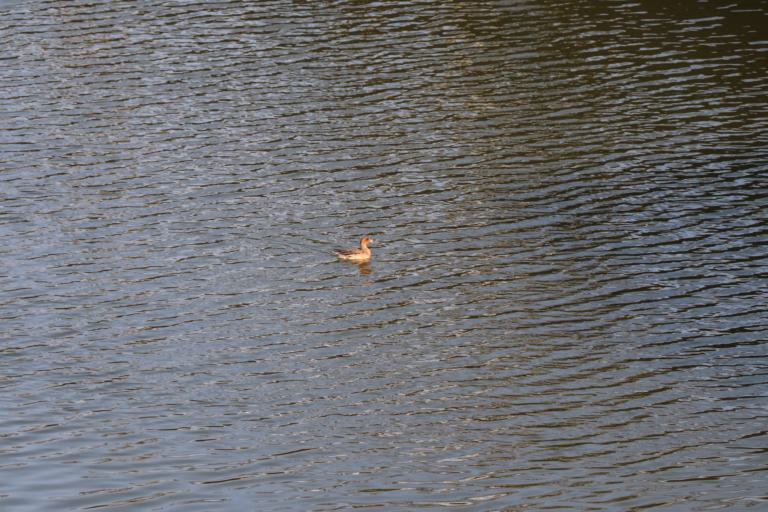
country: JP
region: Nagasaki
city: Shimabara
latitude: 32.7883
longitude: 130.3661
